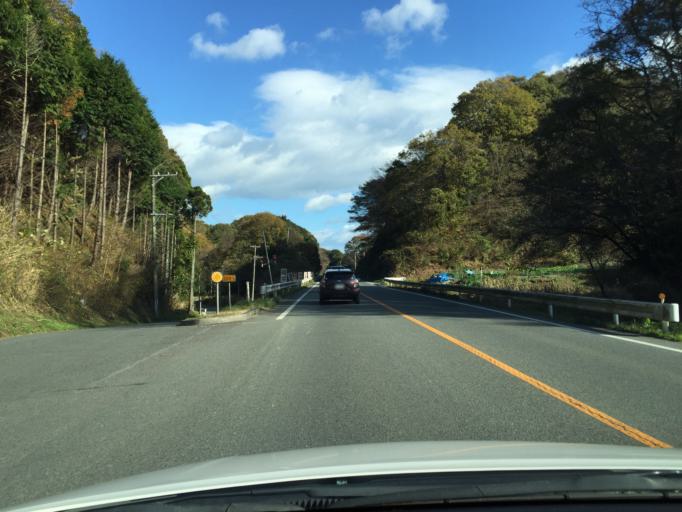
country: JP
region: Fukushima
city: Iwaki
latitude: 37.1875
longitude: 140.9965
